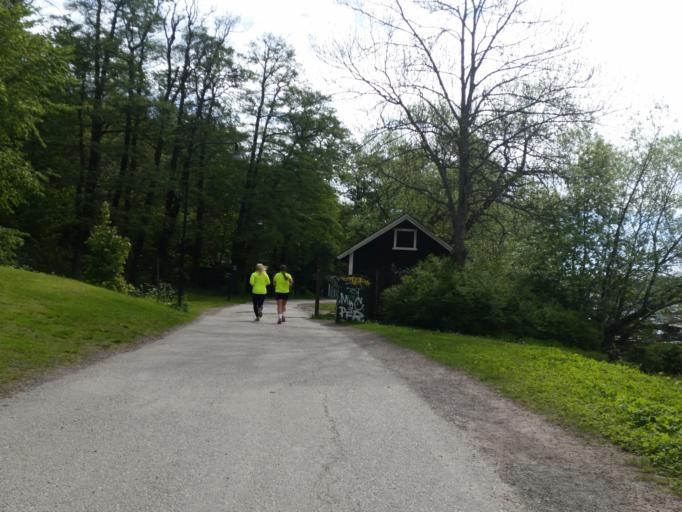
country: SE
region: Stockholm
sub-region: Stockholms Kommun
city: Arsta
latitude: 59.3087
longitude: 18.0496
